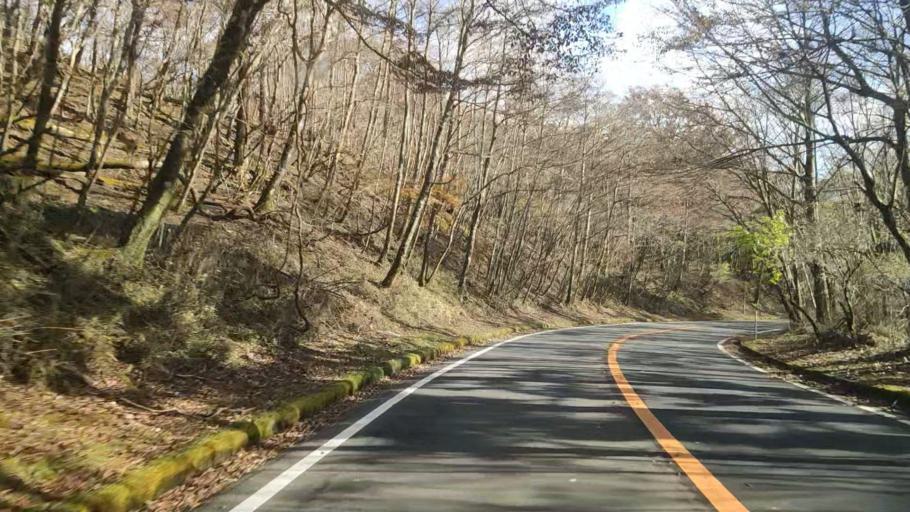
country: JP
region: Shizuoka
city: Fuji
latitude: 35.3028
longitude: 138.7528
